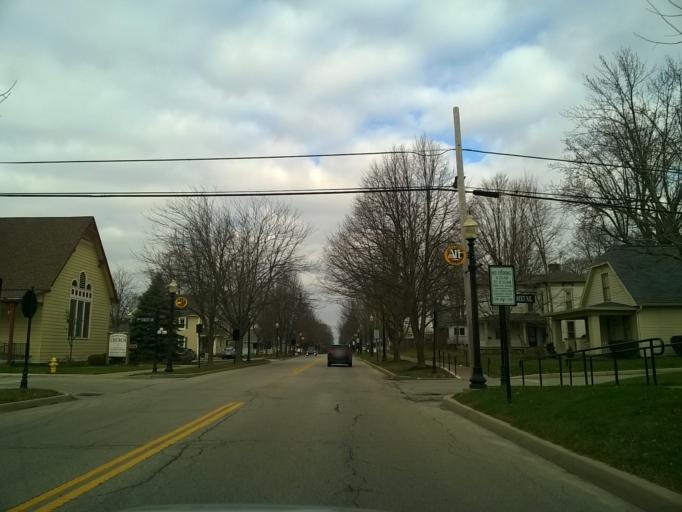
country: US
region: Indiana
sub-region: Hamilton County
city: Carmel
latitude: 39.9817
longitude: -86.1271
